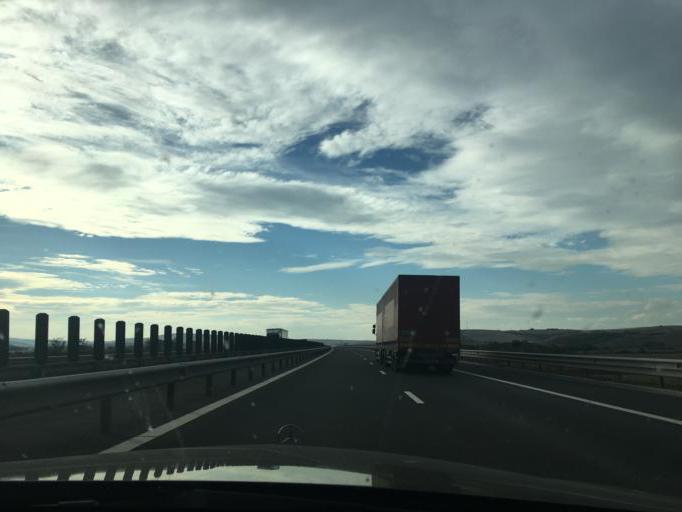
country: RO
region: Sibiu
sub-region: Oras Miercurea Sibiului
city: Miercurea Sibiului
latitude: 45.8963
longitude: 23.8052
